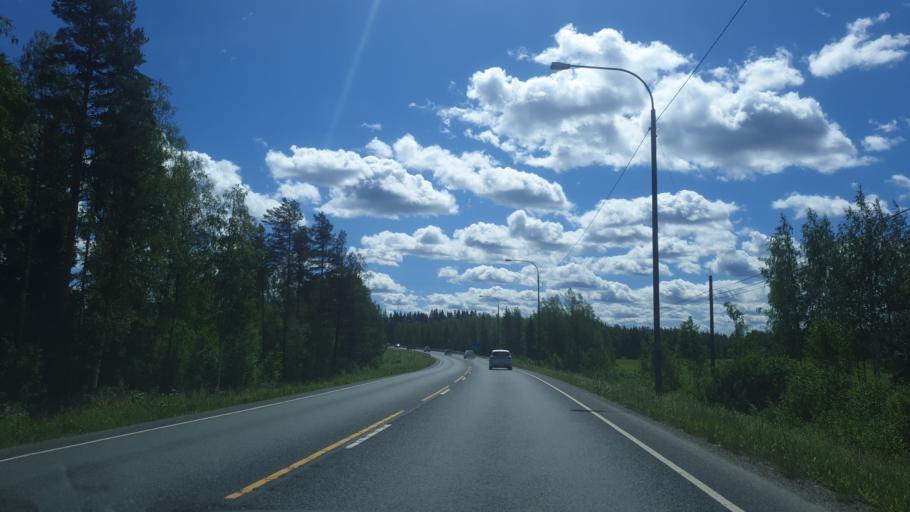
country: FI
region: Northern Savo
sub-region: Varkaus
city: Leppaevirta
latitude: 62.5474
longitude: 27.6235
